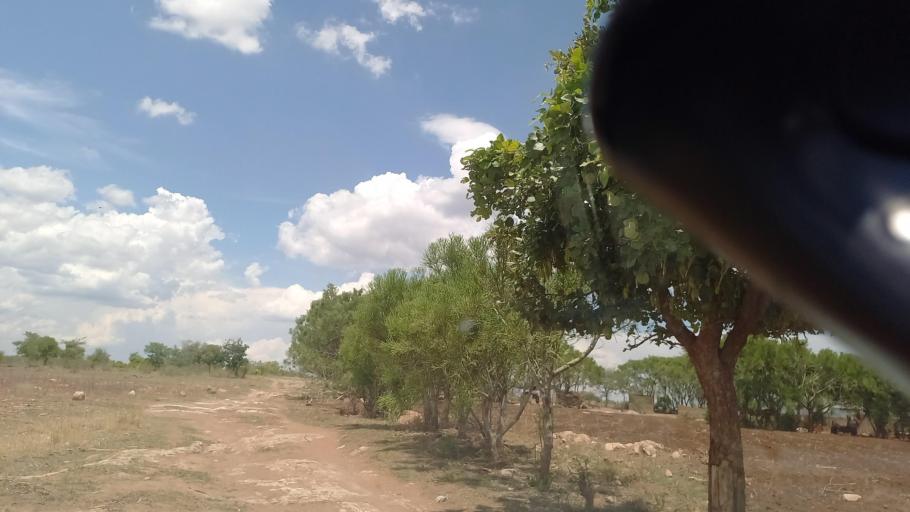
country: ZM
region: Southern
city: Mazabuka
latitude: -16.1104
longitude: 27.8160
